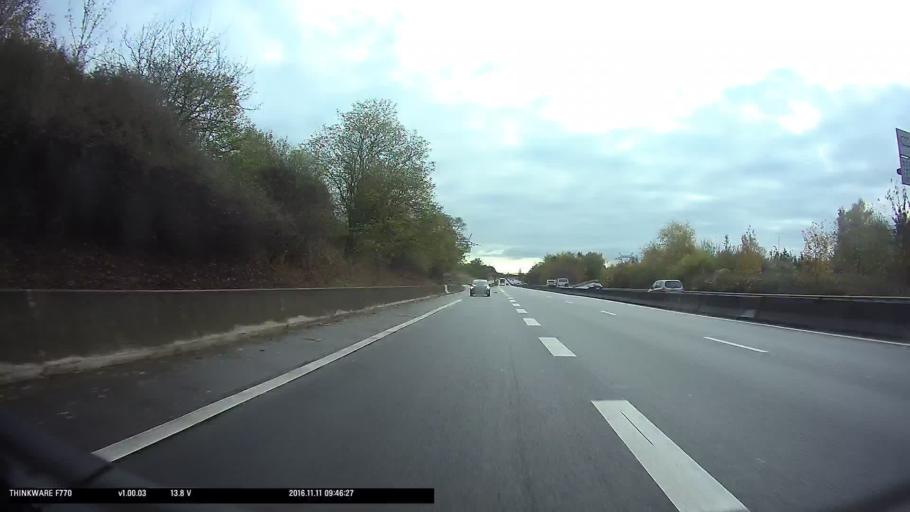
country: FR
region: Ile-de-France
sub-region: Departement du Val-d'Oise
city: Osny
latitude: 49.0569
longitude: 2.0426
